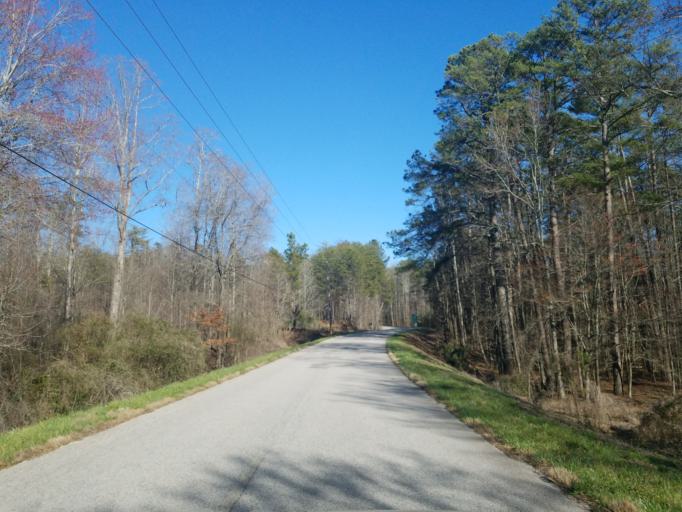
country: US
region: Georgia
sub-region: Pickens County
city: Nelson
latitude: 34.4660
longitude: -84.2580
